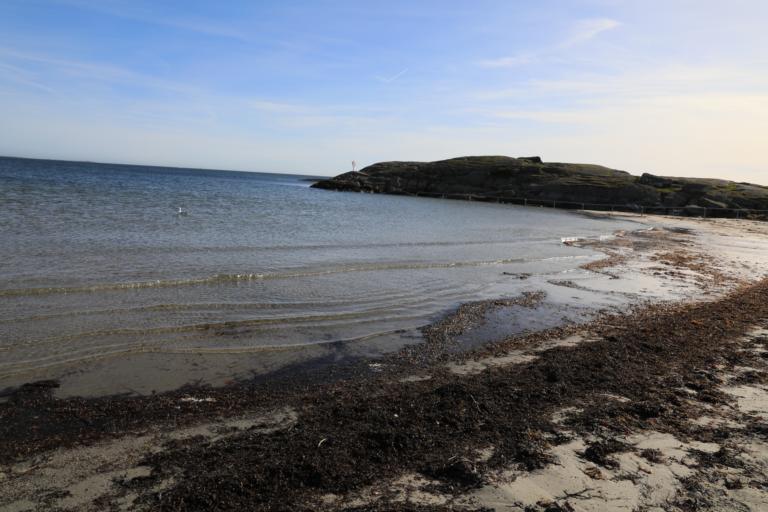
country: SE
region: Halland
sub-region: Varbergs Kommun
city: Varberg
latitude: 57.1180
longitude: 12.2021
